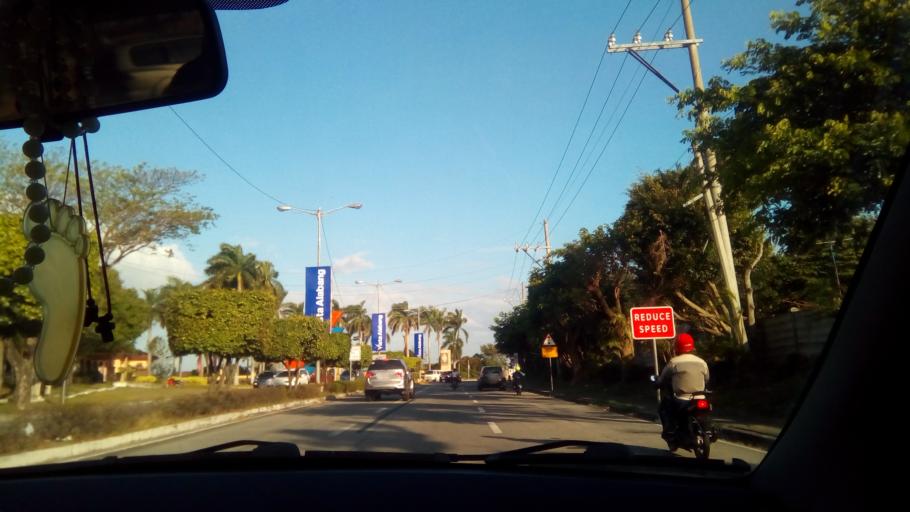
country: PH
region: Calabarzon
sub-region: Province of Laguna
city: San Pedro
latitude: 14.3838
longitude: 121.0113
